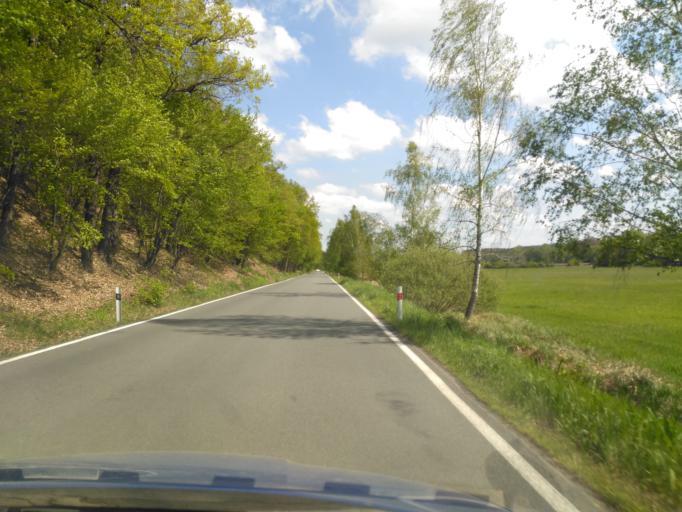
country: CZ
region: Central Bohemia
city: Lochovice
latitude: 49.8334
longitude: 13.9657
